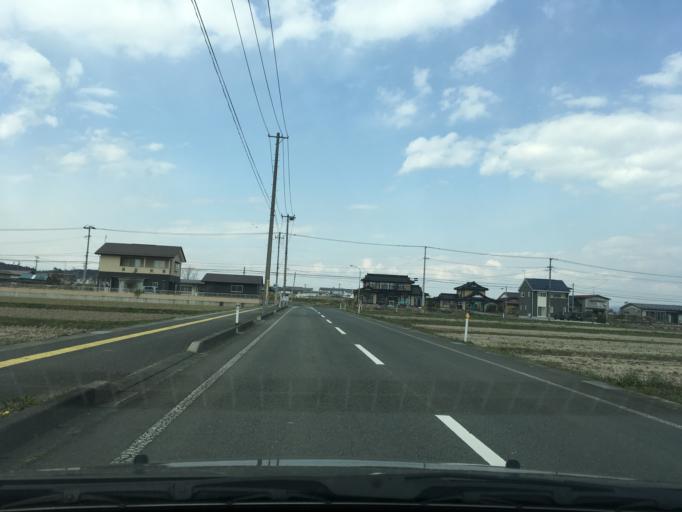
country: JP
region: Iwate
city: Mizusawa
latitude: 39.0571
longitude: 141.1318
